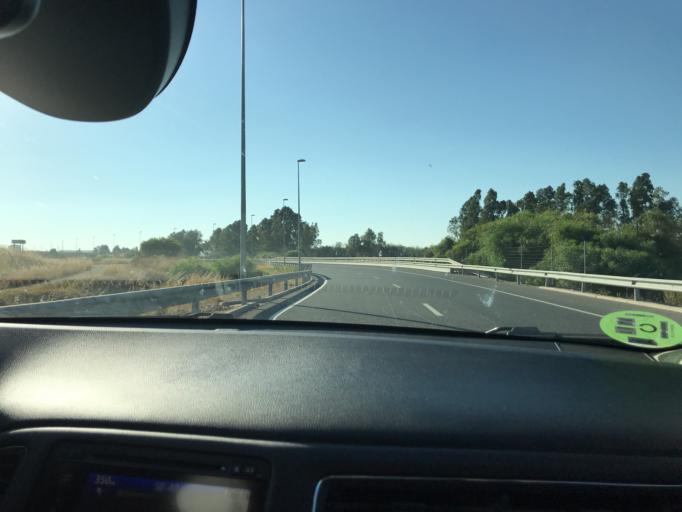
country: ES
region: Andalusia
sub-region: Provincia de Sevilla
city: Alcala de Guadaira
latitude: 37.4325
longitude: -5.8388
